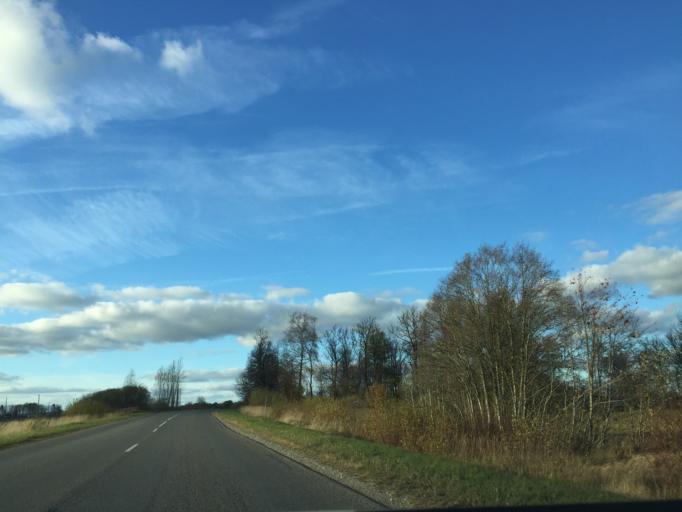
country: LV
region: Tukuma Rajons
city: Tukums
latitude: 56.9856
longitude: 23.1049
